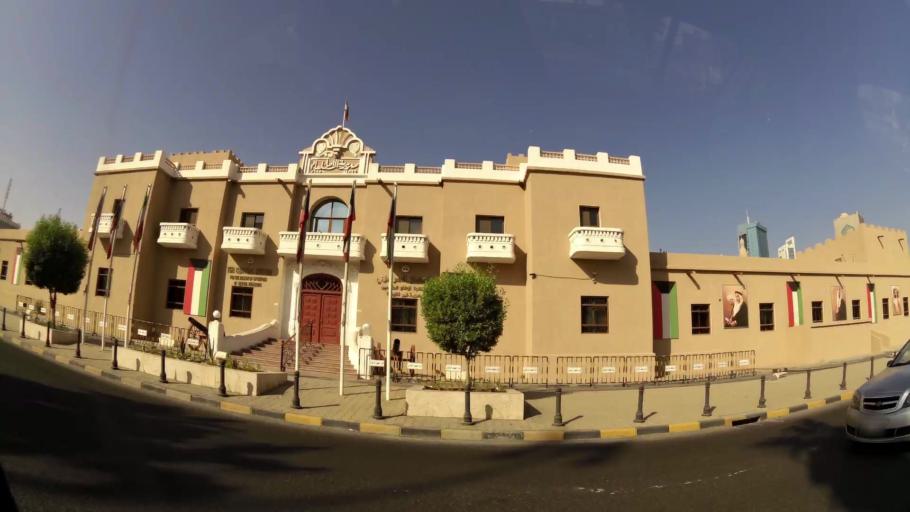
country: KW
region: Al Asimah
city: Kuwait City
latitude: 29.3655
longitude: 47.9742
